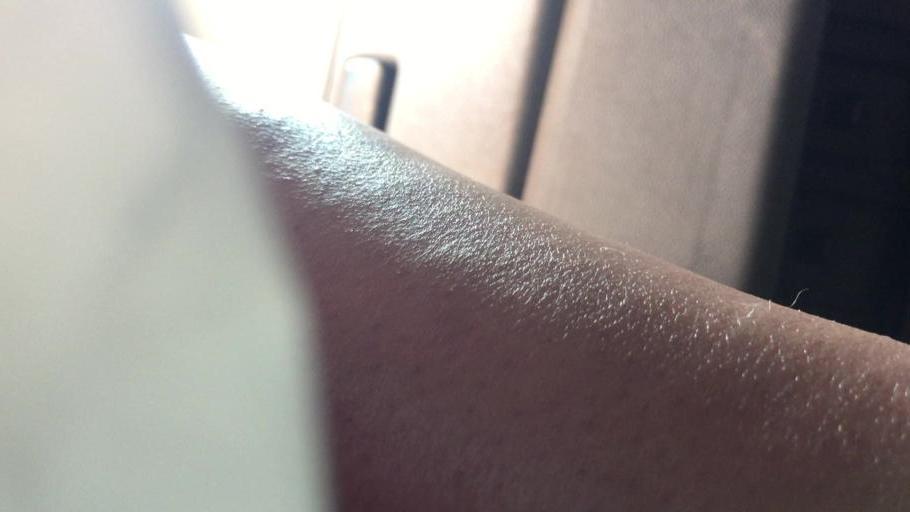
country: US
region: Georgia
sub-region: Carroll County
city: Carrollton
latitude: 33.5925
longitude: -85.0417
